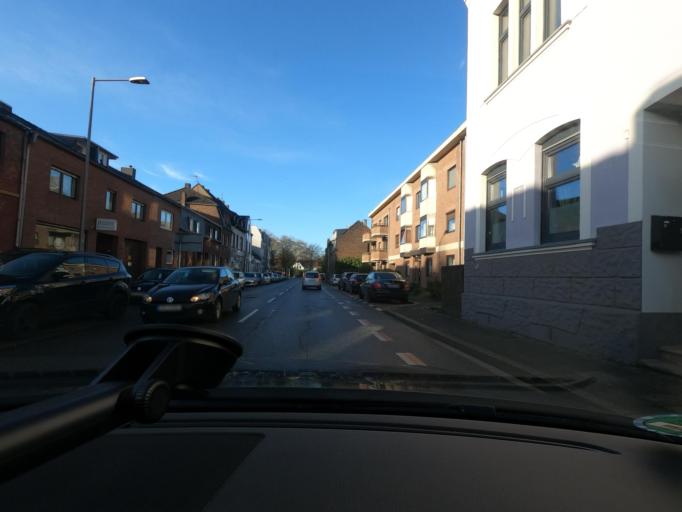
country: DE
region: North Rhine-Westphalia
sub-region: Regierungsbezirk Dusseldorf
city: Krefeld
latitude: 51.3476
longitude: 6.6113
